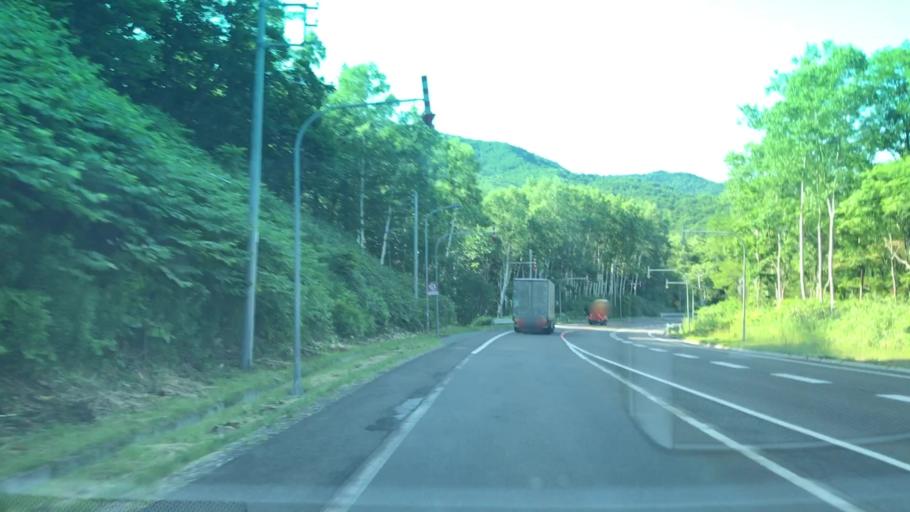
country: JP
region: Hokkaido
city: Yoichi
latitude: 43.0695
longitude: 140.6996
